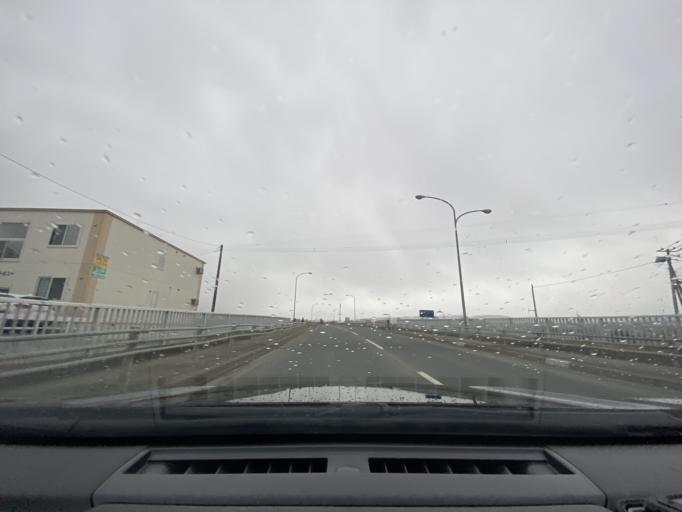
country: JP
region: Hokkaido
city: Kitami
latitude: 43.7987
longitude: 143.9134
